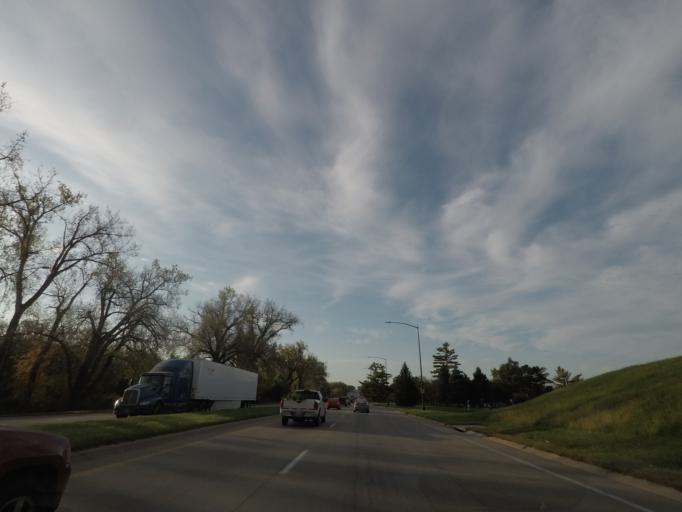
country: US
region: Iowa
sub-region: Polk County
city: Des Moines
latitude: 41.5768
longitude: -93.6450
